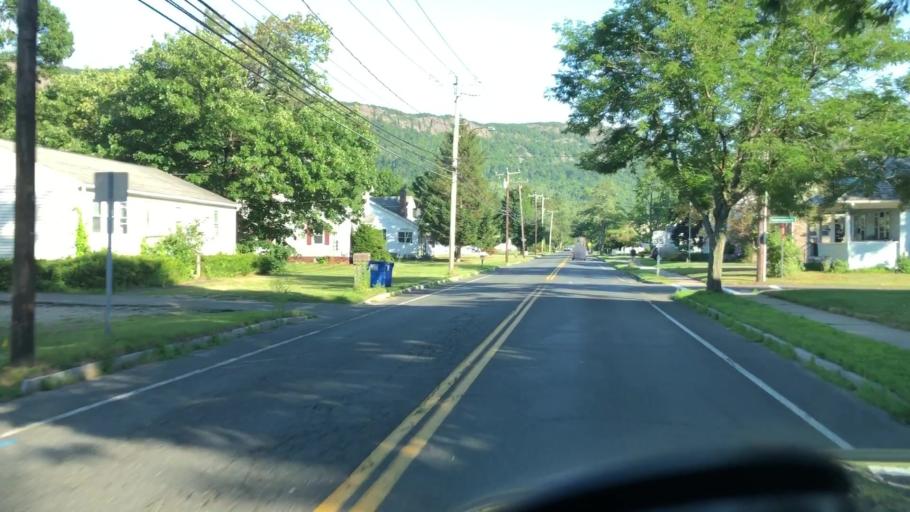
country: US
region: Massachusetts
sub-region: Hampshire County
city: Easthampton
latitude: 42.2592
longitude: -72.6602
